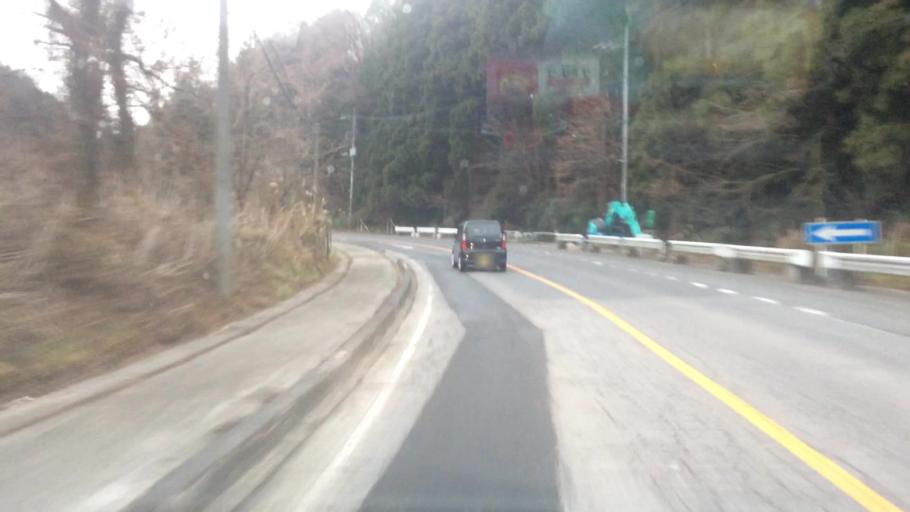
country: JP
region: Tochigi
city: Imaichi
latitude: 36.7324
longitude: 139.7465
